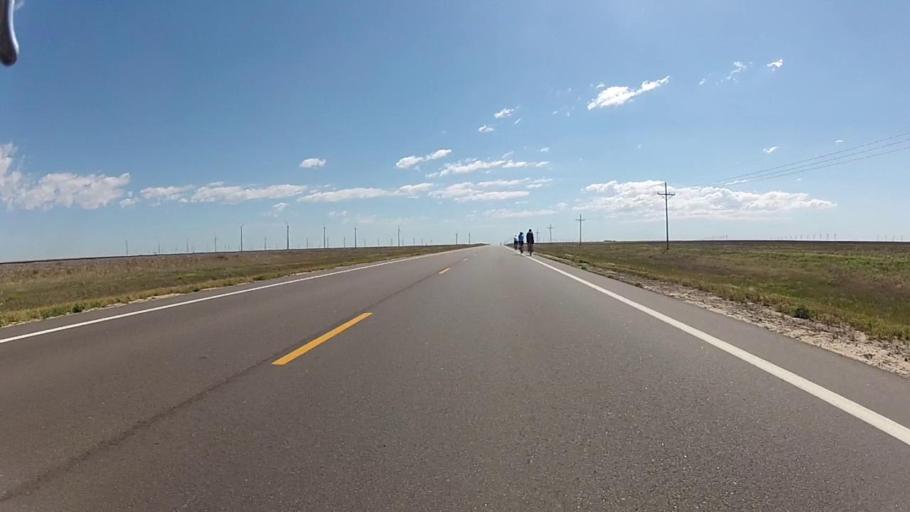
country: US
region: Kansas
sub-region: Gray County
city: Cimarron
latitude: 37.6048
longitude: -100.4230
